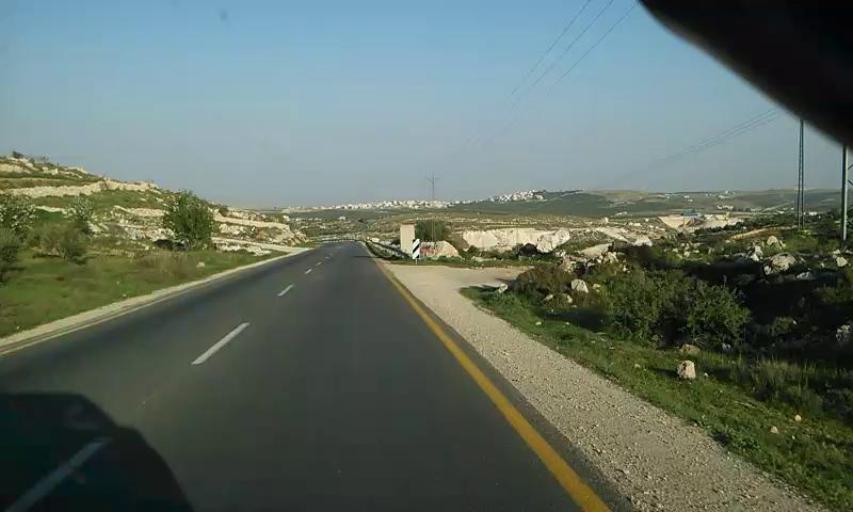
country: PS
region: West Bank
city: Jurat ash Sham`ah
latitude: 31.6473
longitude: 35.1796
